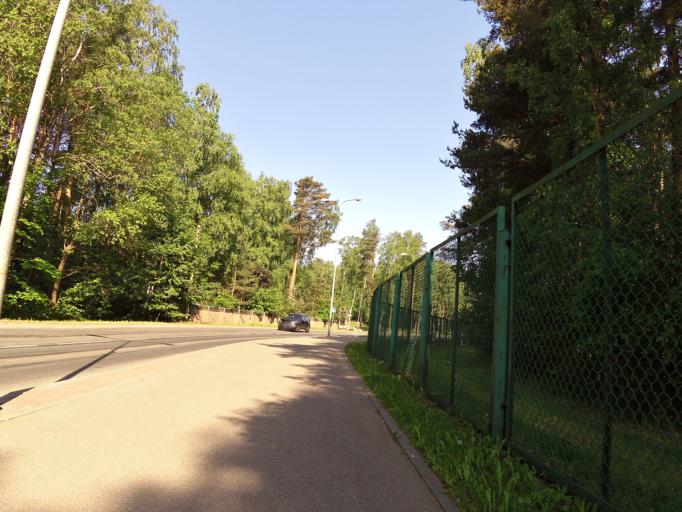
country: EE
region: Harju
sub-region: Saue vald
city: Laagri
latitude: 59.4337
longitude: 24.6303
